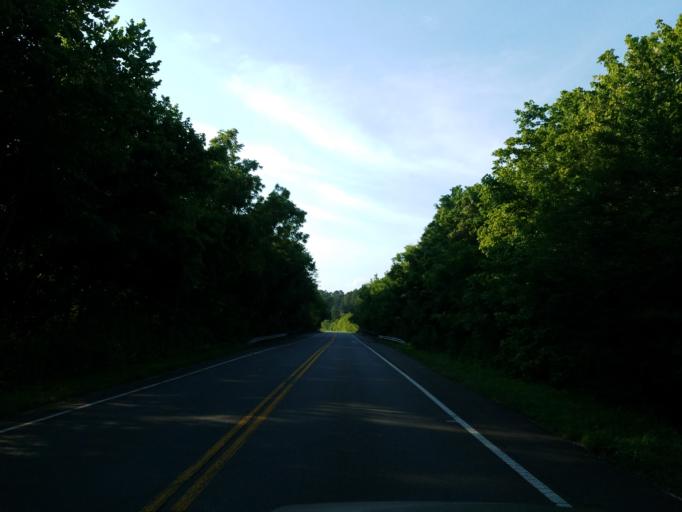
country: US
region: Georgia
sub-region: Pickens County
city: Jasper
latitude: 34.5216
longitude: -84.5239
